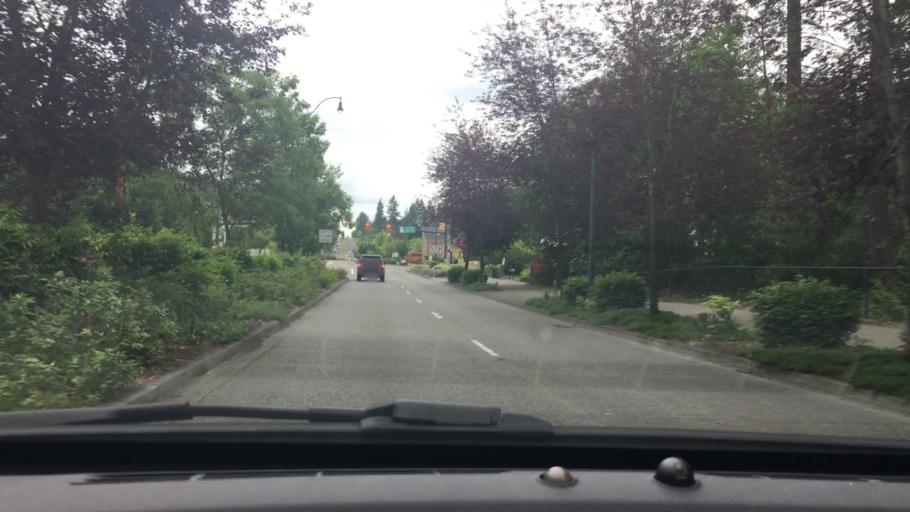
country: US
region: Washington
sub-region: King County
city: City of Sammamish
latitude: 47.6118
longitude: -122.0354
